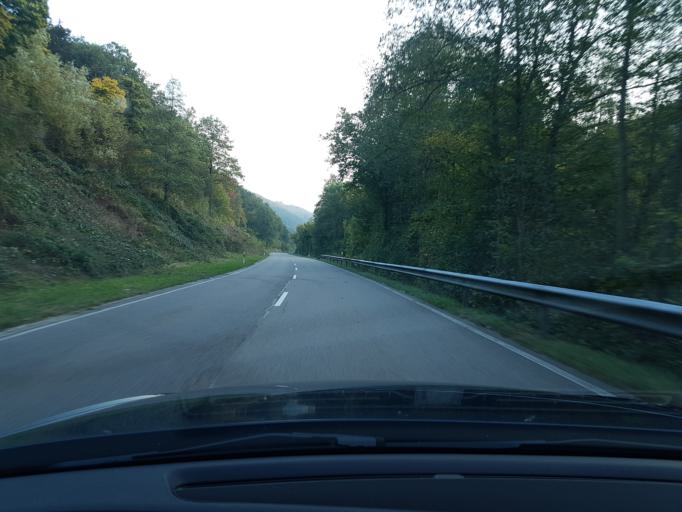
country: DE
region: Baden-Wuerttemberg
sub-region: Karlsruhe Region
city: Eberbach
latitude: 49.4908
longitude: 8.9641
